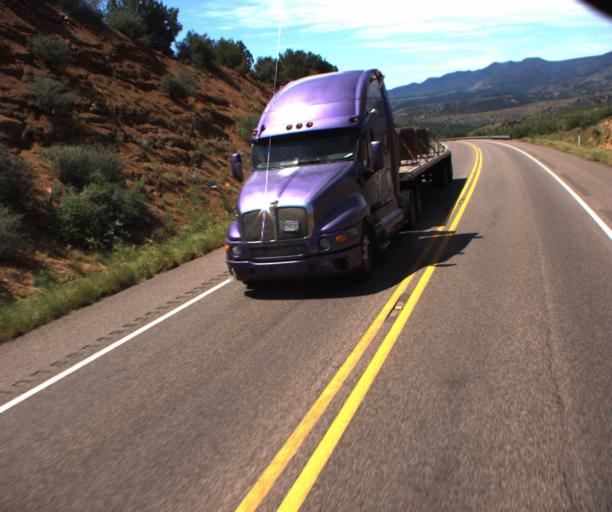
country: US
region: Arizona
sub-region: Gila County
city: Globe
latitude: 33.6100
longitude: -110.6260
